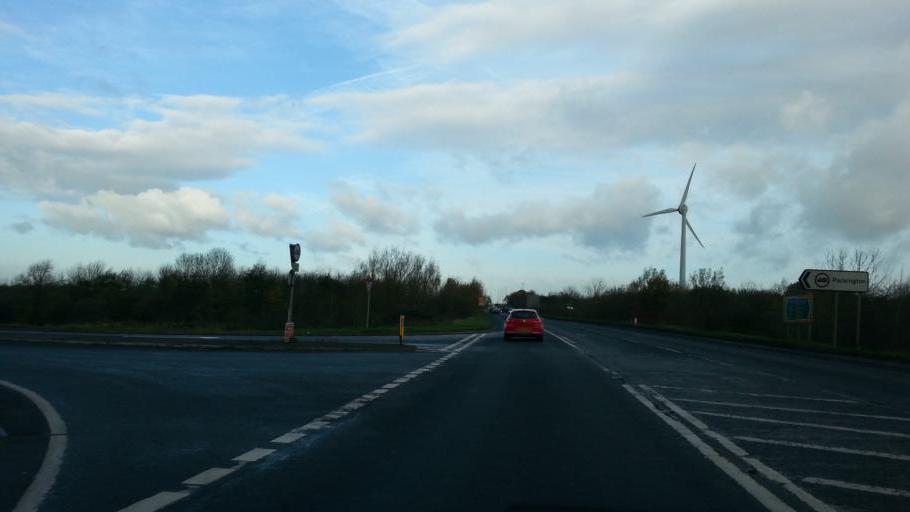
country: GB
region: England
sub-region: Leicestershire
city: Ashby de la Zouch
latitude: 52.7448
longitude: -1.4411
